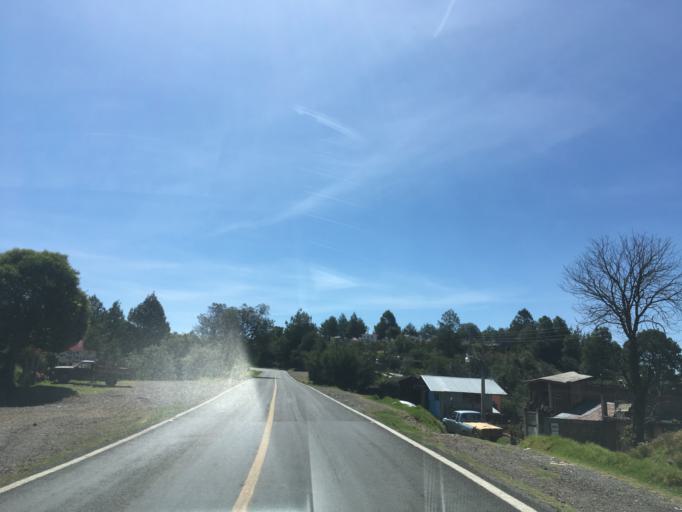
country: MX
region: Michoacan
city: Tzitzio
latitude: 19.6740
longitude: -100.8559
